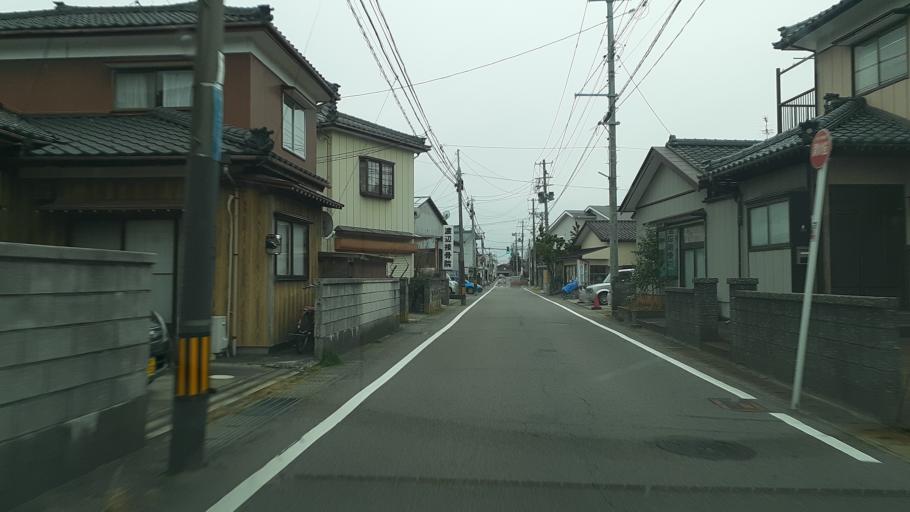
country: JP
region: Niigata
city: Niigata-shi
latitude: 37.8575
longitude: 139.0345
